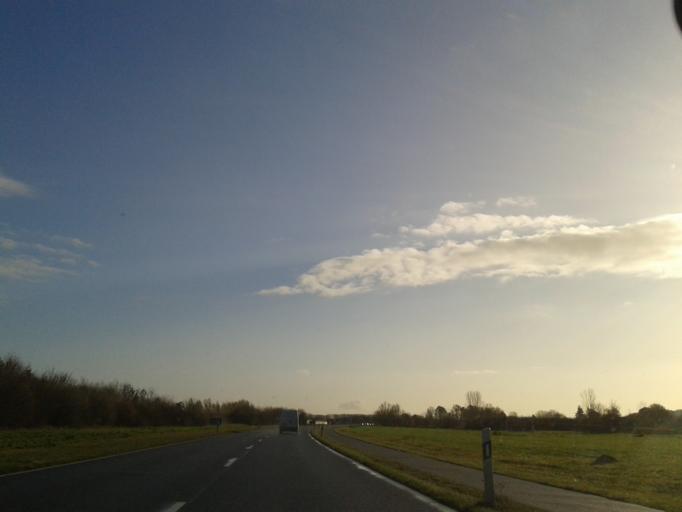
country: DE
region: North Rhine-Westphalia
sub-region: Regierungsbezirk Dusseldorf
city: Xanten
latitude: 51.6714
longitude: 6.4470
